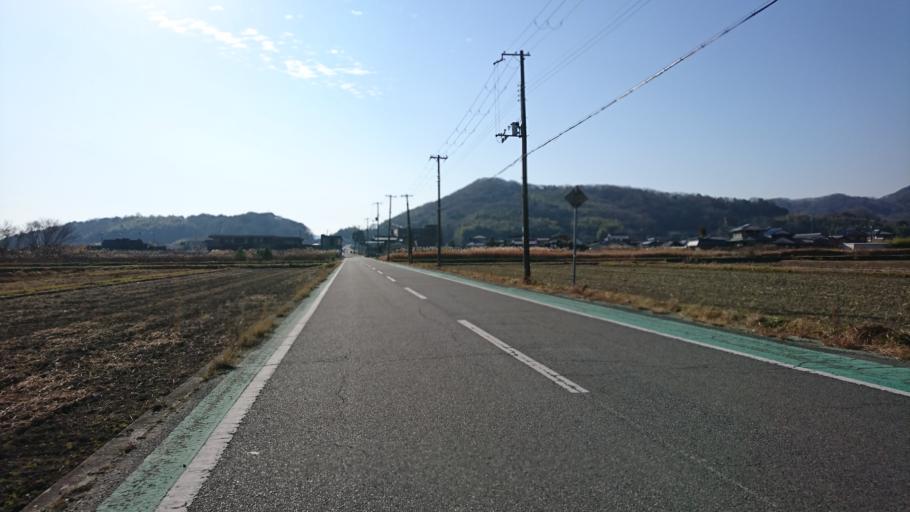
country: JP
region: Hyogo
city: Kakogawacho-honmachi
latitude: 34.8309
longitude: 134.8345
